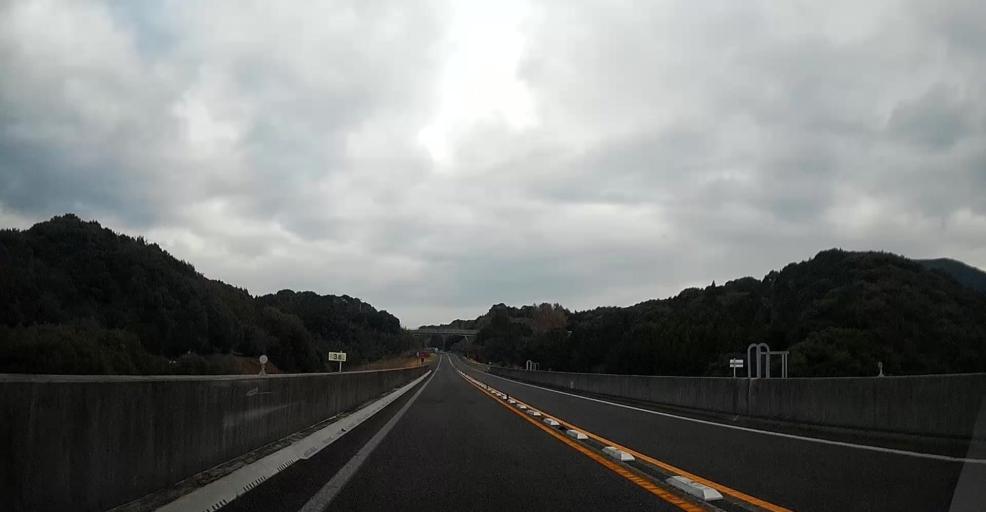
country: JP
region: Kumamoto
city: Hondo
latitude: 32.5081
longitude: 130.3422
